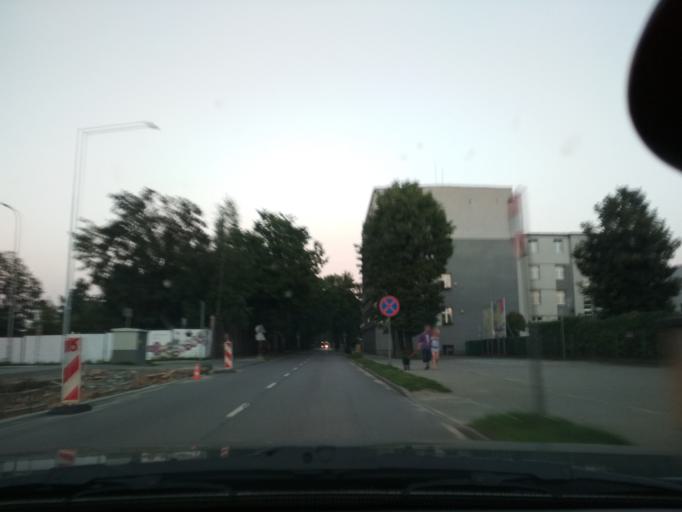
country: PL
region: Silesian Voivodeship
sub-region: Powiat zawiercianski
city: Zawiercie
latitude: 50.4854
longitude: 19.4341
